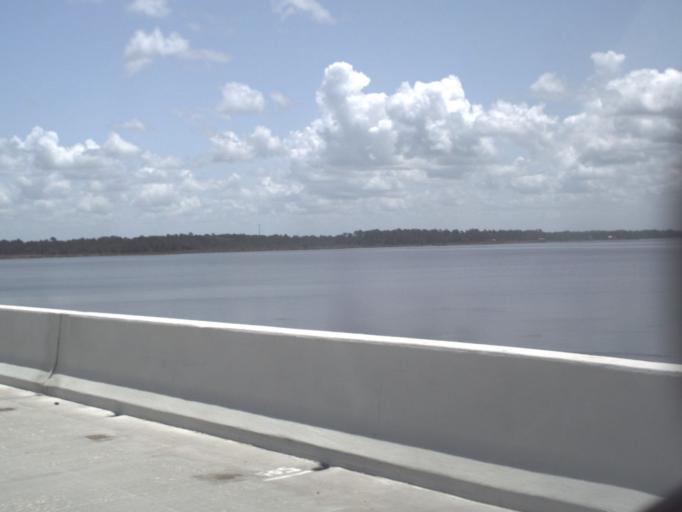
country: US
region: Florida
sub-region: Walton County
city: Freeport
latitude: 30.4238
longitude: -86.1572
